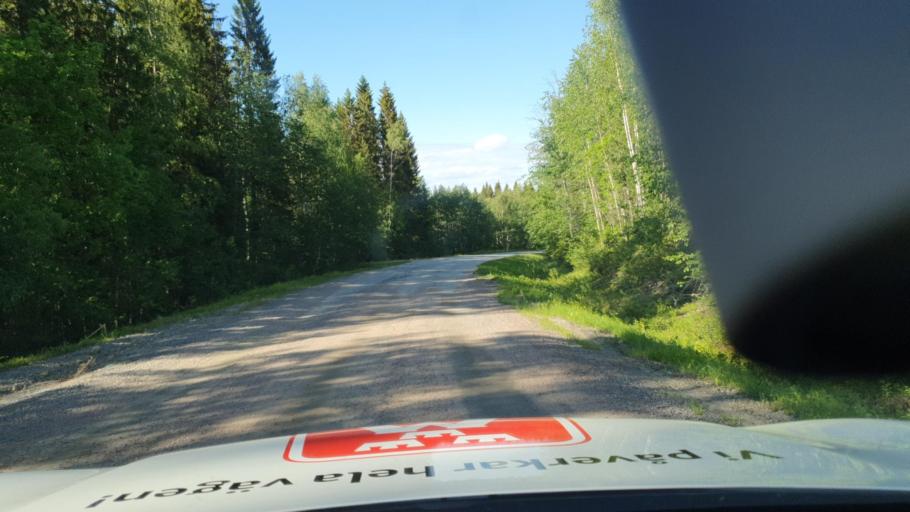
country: SE
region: Vaesterbotten
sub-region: Vannas Kommun
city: Vaennaes
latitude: 63.8463
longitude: 19.6218
